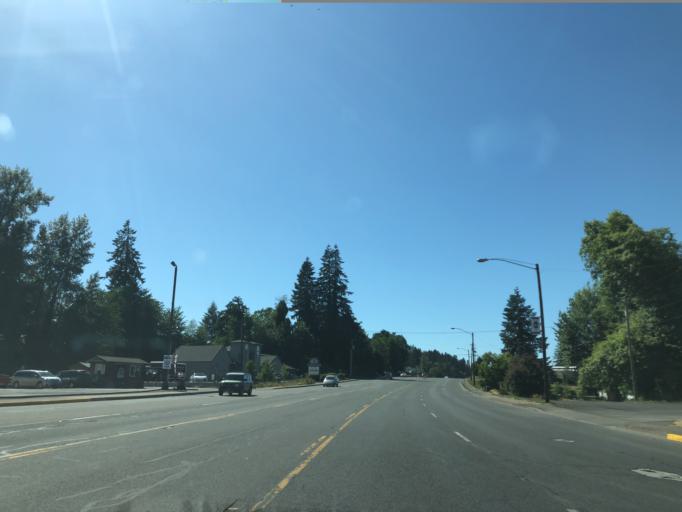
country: US
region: Oregon
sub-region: Linn County
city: Sweet Home
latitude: 44.3980
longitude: -122.7374
